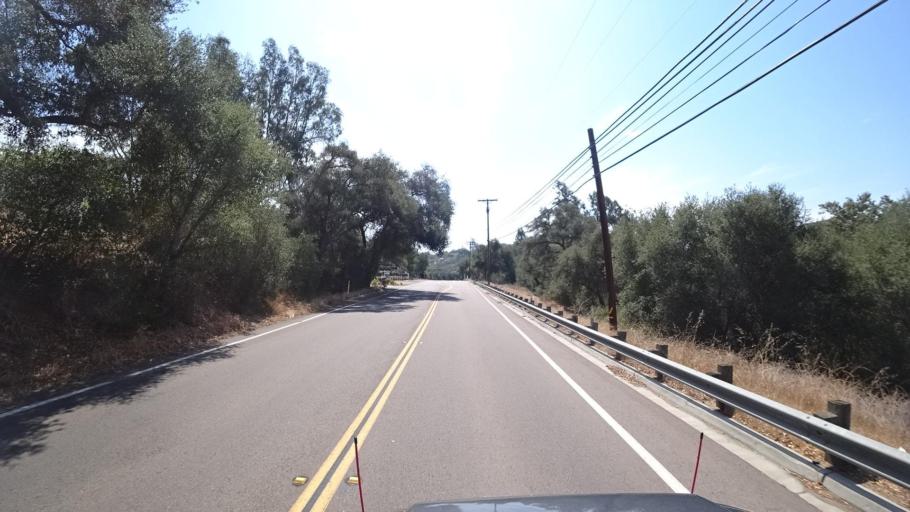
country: US
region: California
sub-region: San Diego County
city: Hidden Meadows
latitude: 33.1738
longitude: -117.1062
